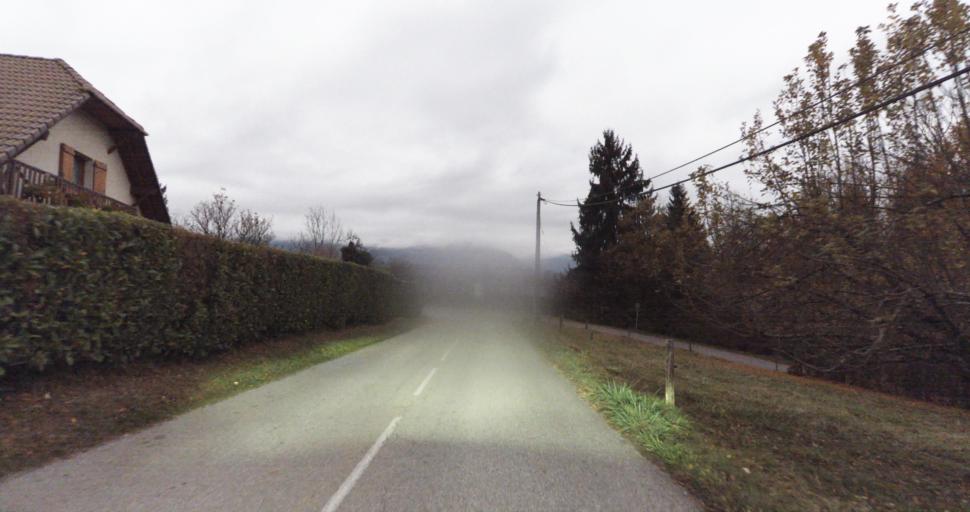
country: FR
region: Rhone-Alpes
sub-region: Departement de la Haute-Savoie
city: Alby-sur-Cheran
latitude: 45.8311
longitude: 6.0186
